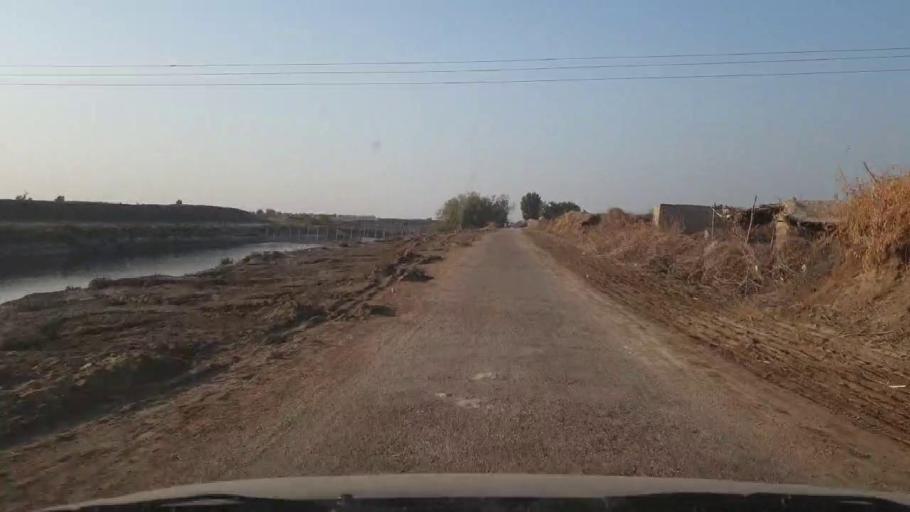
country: PK
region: Sindh
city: Samaro
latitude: 25.2889
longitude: 69.3341
